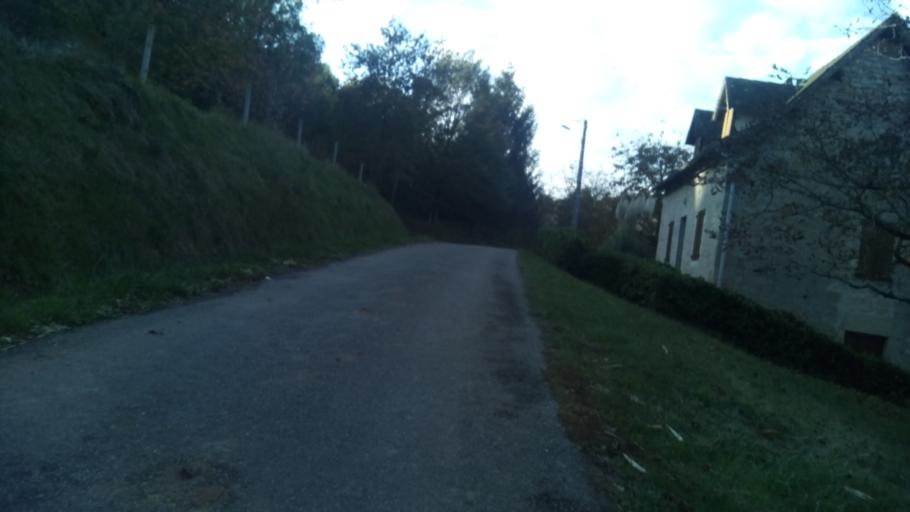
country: FR
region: Midi-Pyrenees
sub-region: Departement du Lot
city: Cajarc
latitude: 44.4727
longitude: 1.8290
